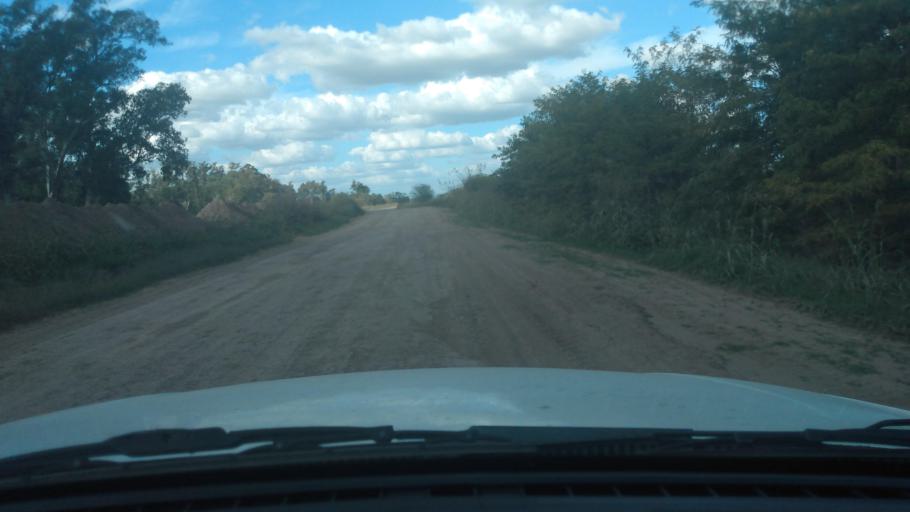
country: AR
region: Buenos Aires
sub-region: Partido de Navarro
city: Navarro
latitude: -35.0123
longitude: -59.4932
